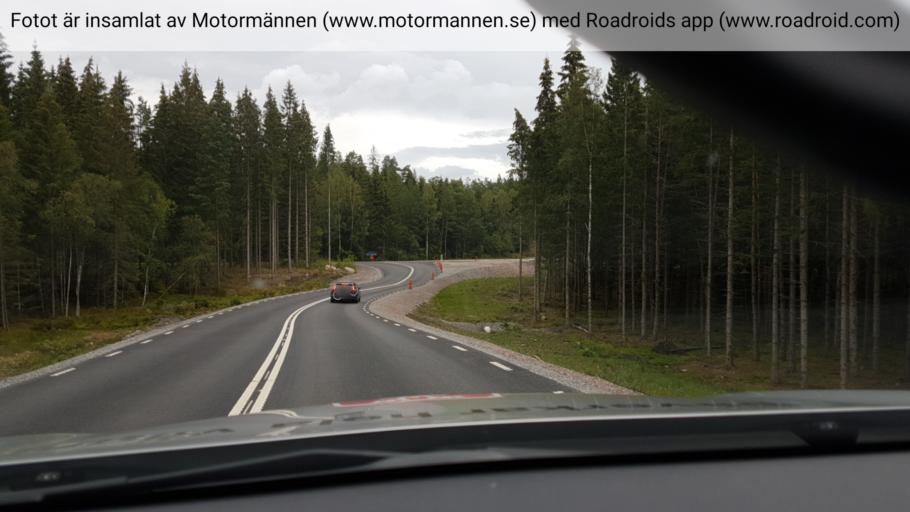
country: SE
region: Vaestra Goetaland
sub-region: Vargarda Kommun
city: Jonstorp
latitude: 57.9829
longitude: 12.7184
